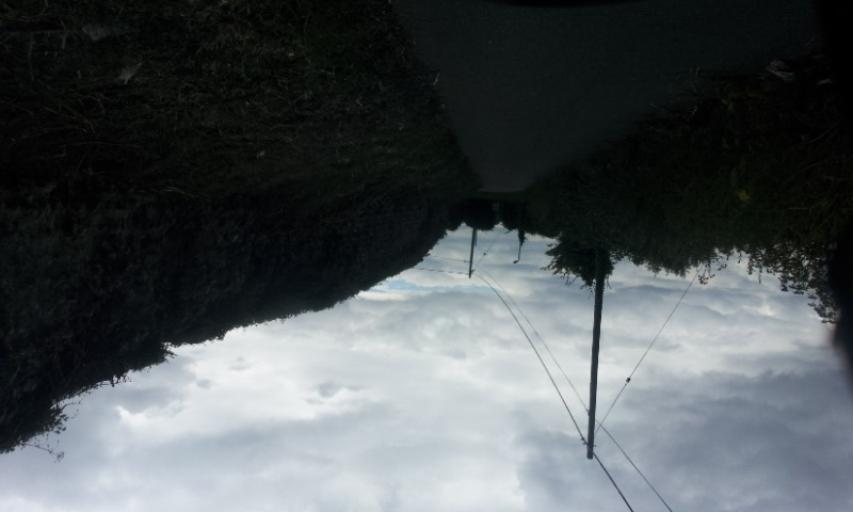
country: GB
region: England
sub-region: Kent
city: Herne Bay
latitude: 51.3791
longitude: 1.2012
